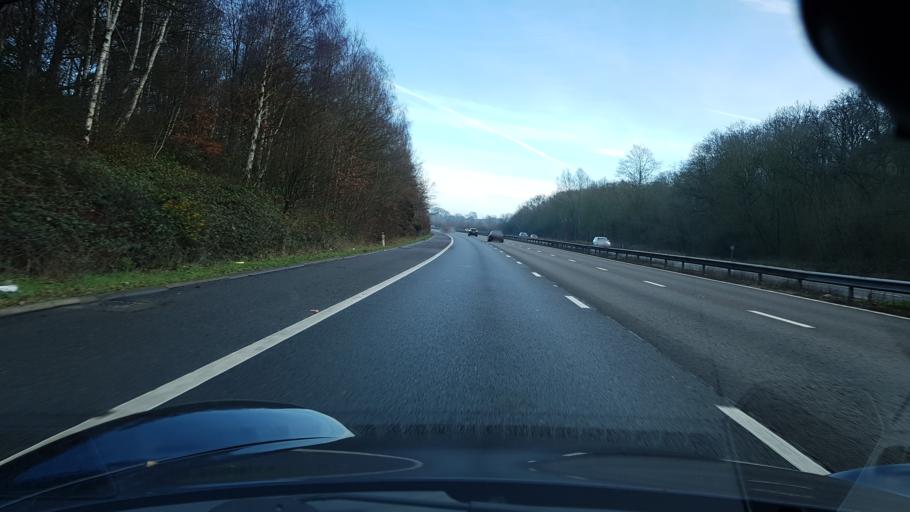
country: GB
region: England
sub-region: Surrey
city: Hinchley Wood
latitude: 51.3498
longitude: -0.3375
